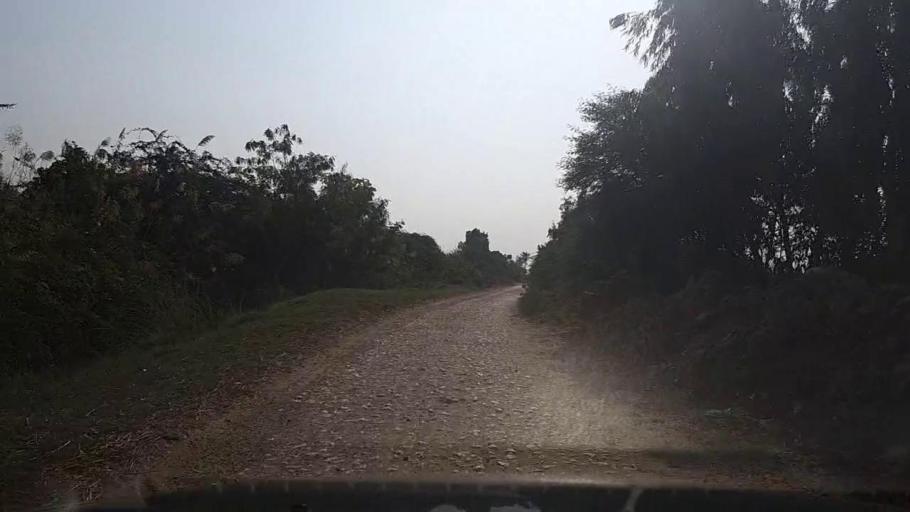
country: PK
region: Sindh
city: Mirpur Sakro
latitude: 24.6257
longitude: 67.7547
